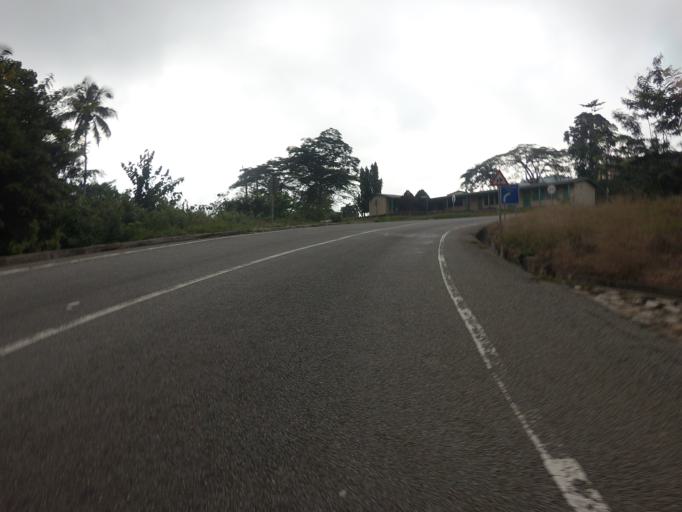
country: GH
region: Volta
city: Kpandu
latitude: 6.8207
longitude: 0.4242
